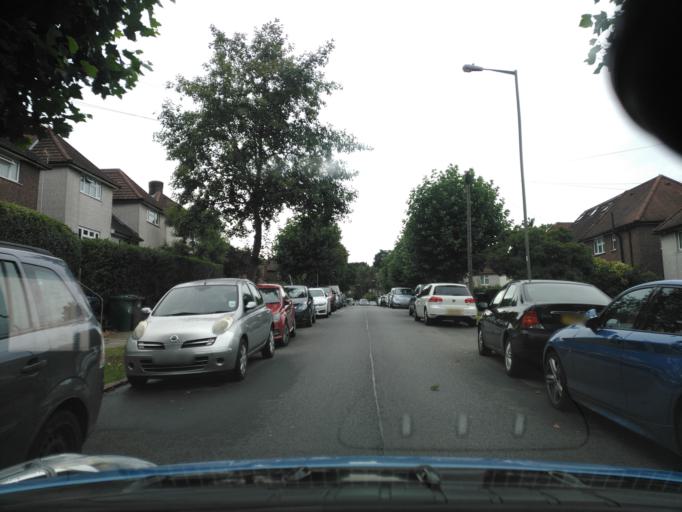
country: GB
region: England
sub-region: Greater London
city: High Barnet
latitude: 51.6485
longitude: -0.2182
